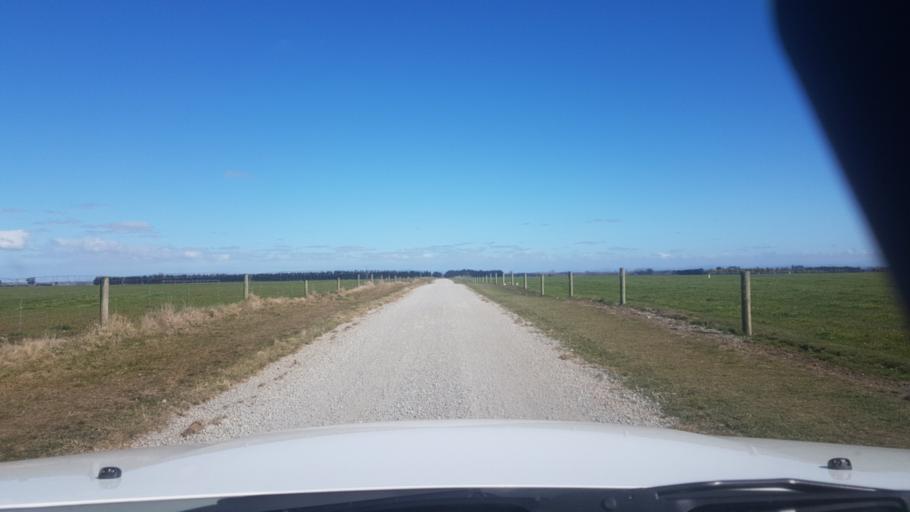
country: NZ
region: Canterbury
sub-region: Timaru District
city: Pleasant Point
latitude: -44.1381
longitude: 171.3786
